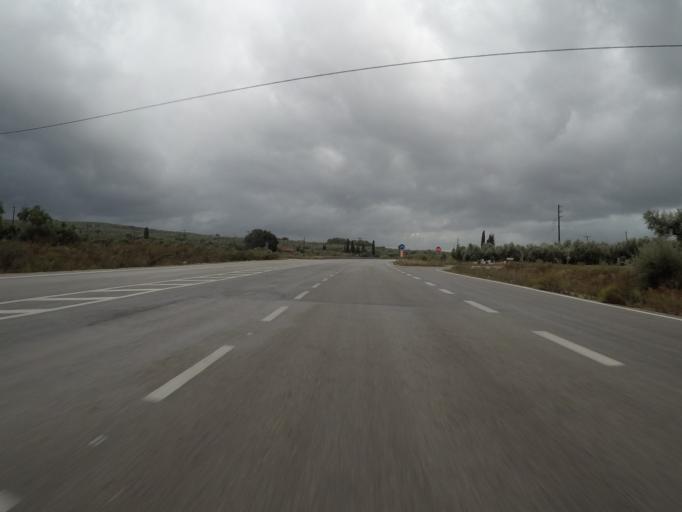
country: GR
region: Peloponnese
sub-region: Nomos Messinias
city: Gargalianoi
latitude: 37.0109
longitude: 21.6554
